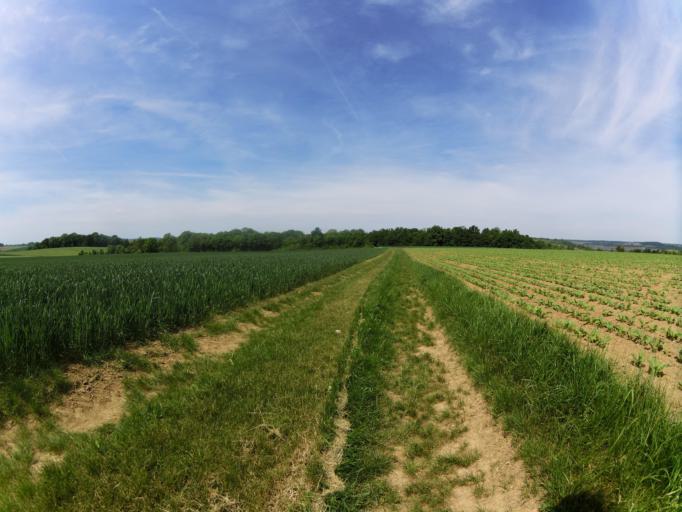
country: DE
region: Bavaria
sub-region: Regierungsbezirk Unterfranken
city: Sommerhausen
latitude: 49.6707
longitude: 10.0238
